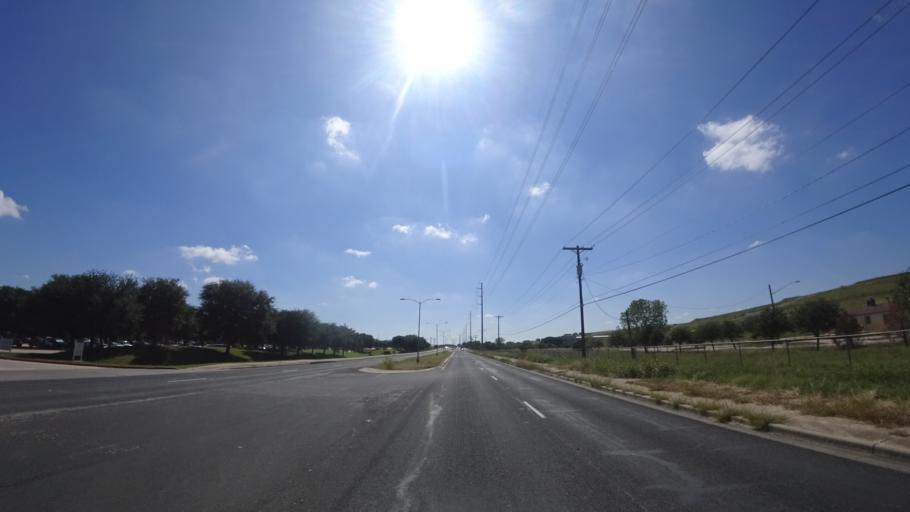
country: US
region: Texas
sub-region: Travis County
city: Manor
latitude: 30.3388
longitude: -97.6188
